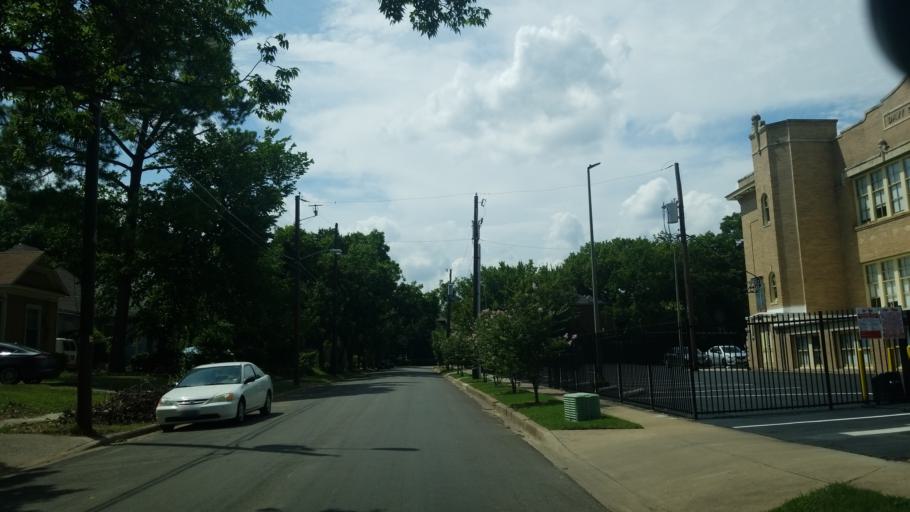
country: US
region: Texas
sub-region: Dallas County
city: Dallas
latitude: 32.7934
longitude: -96.7713
